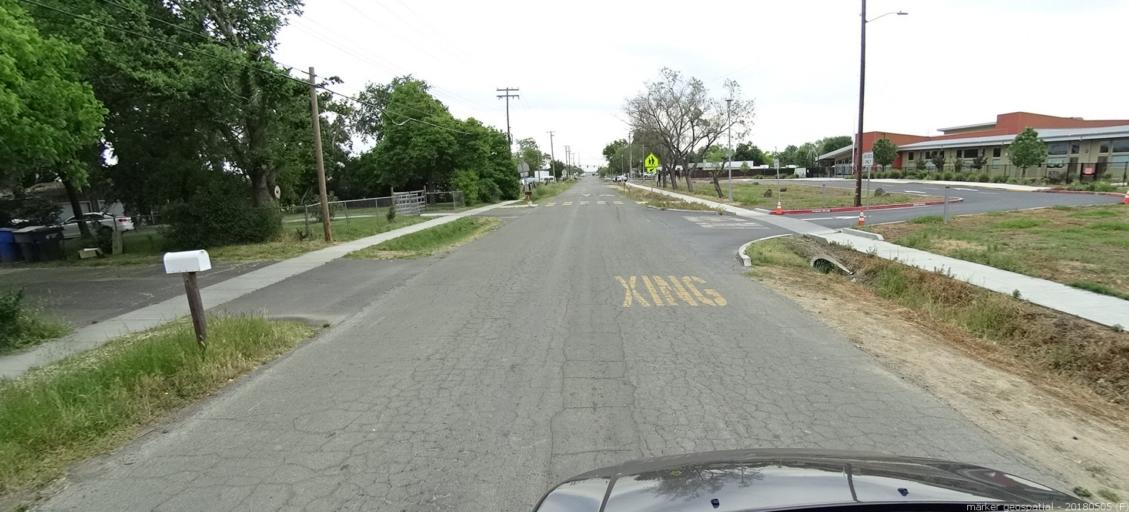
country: US
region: California
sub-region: Sacramento County
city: Rio Linda
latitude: 38.6546
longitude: -121.4332
